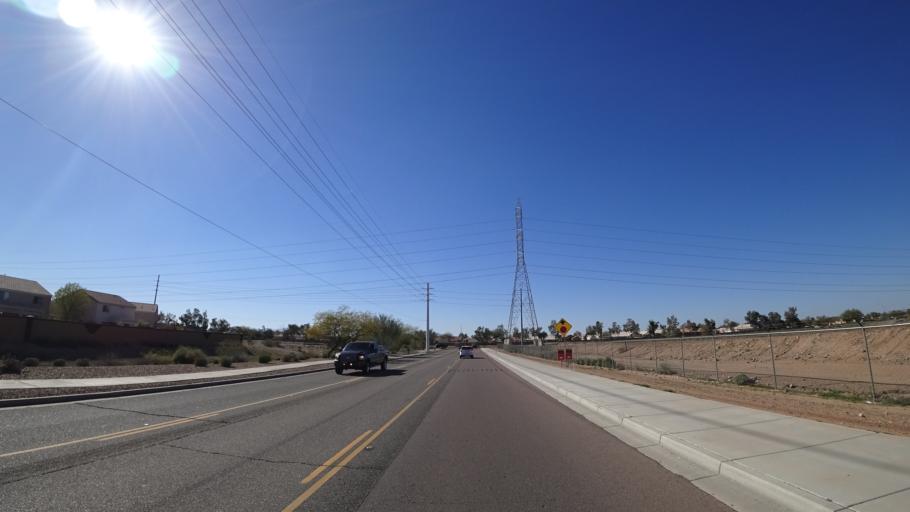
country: US
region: Arizona
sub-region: Maricopa County
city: Surprise
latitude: 33.6525
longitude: -112.3060
